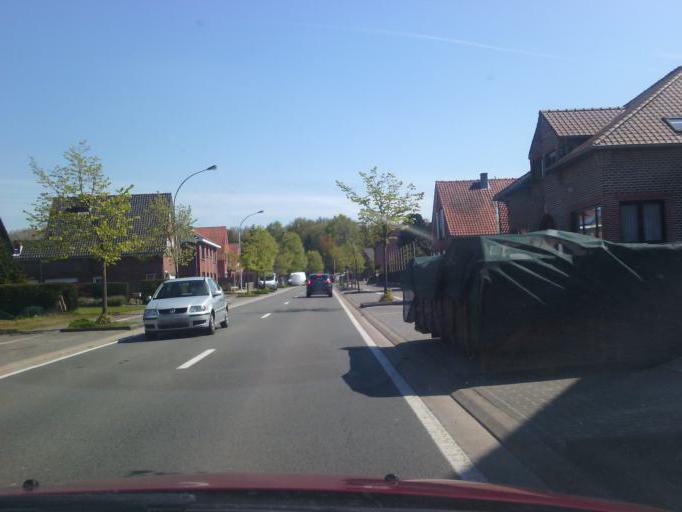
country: BE
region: Flanders
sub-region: Provincie Oost-Vlaanderen
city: Waasmunster
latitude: 51.1344
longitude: 4.0765
